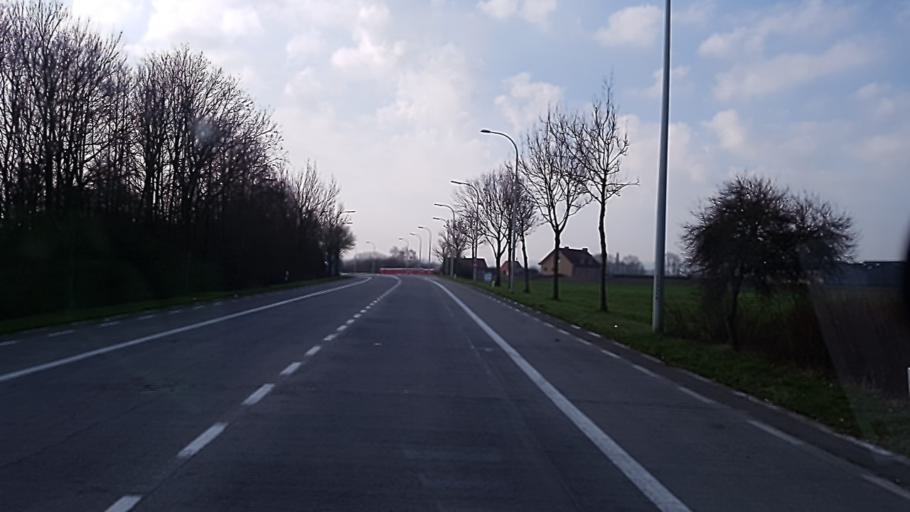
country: BE
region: Flanders
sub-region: Provincie West-Vlaanderen
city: Poperinge
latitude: 50.8534
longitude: 2.7079
